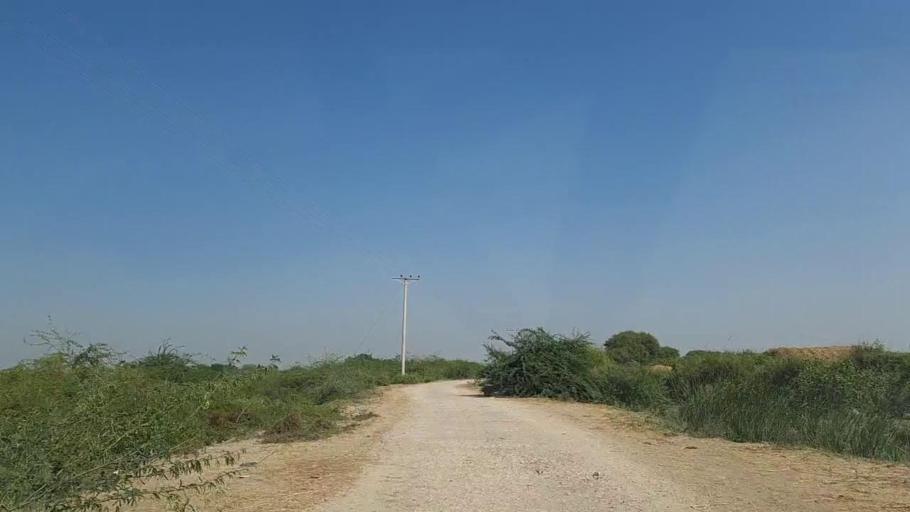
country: PK
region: Sindh
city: Daro Mehar
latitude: 24.7201
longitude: 68.1720
